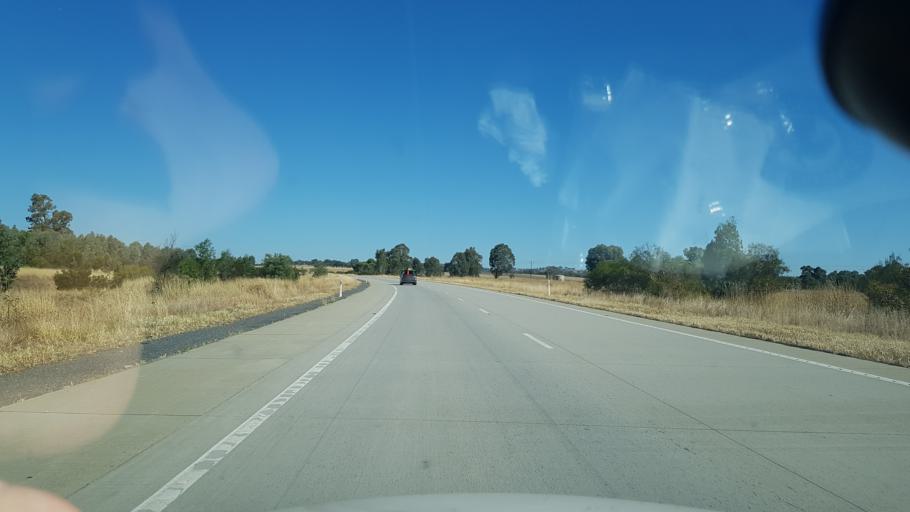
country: AU
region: New South Wales
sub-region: Greater Hume Shire
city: Jindera
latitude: -35.9309
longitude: 147.0035
